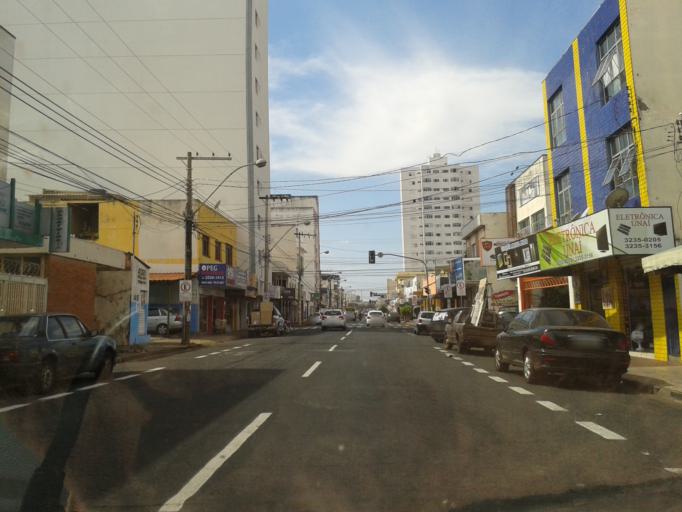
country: BR
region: Minas Gerais
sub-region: Uberlandia
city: Uberlandia
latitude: -18.9114
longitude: -48.2728
